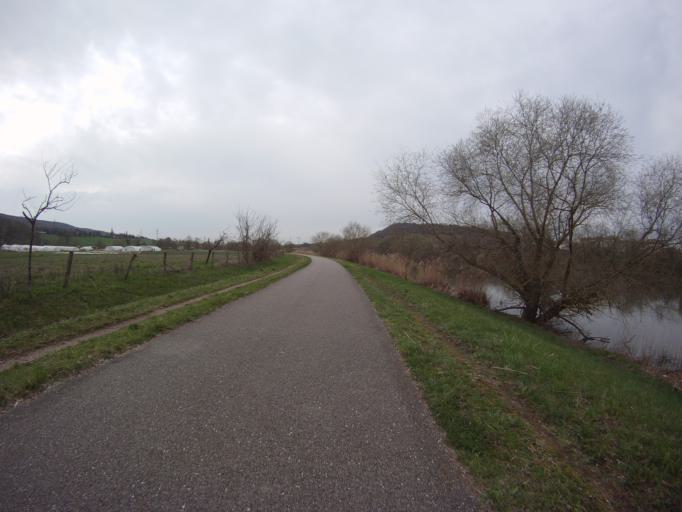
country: FR
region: Lorraine
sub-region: Departement de Meurthe-et-Moselle
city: Champigneulles
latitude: 48.7352
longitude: 6.1721
